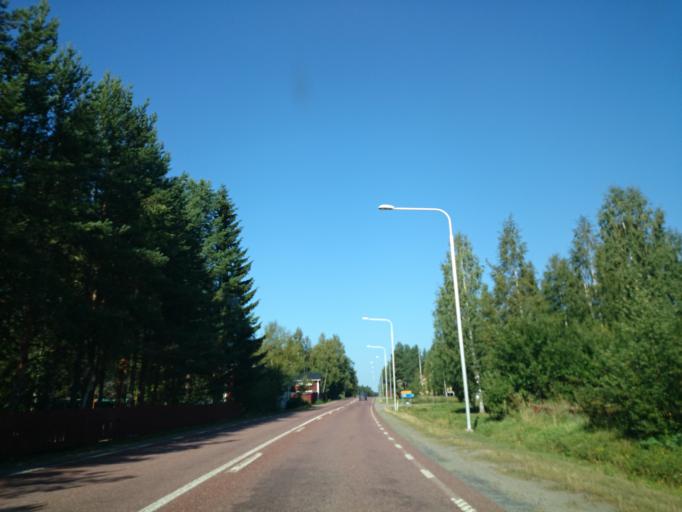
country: SE
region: Gaevleborg
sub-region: Hudiksvalls Kommun
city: Delsbo
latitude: 61.7864
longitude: 16.6132
